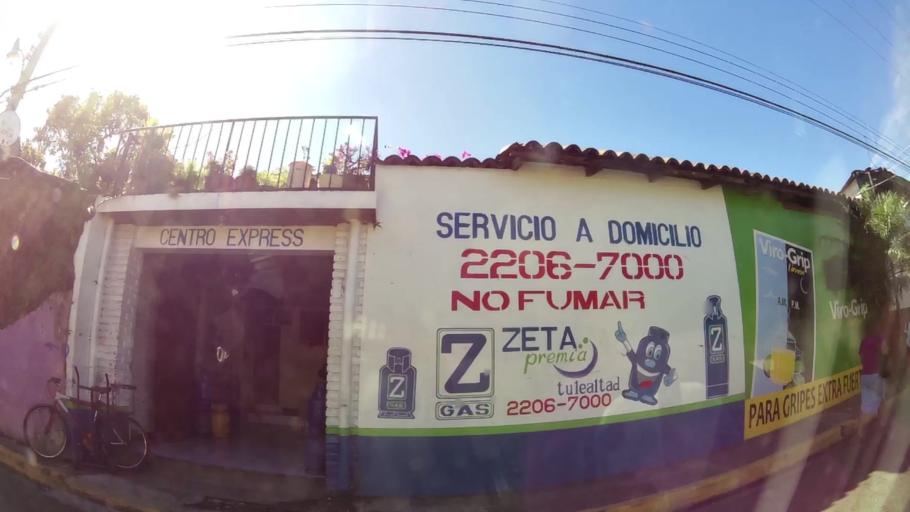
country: SV
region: Sonsonate
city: Juayua
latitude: 13.8435
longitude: -89.7450
